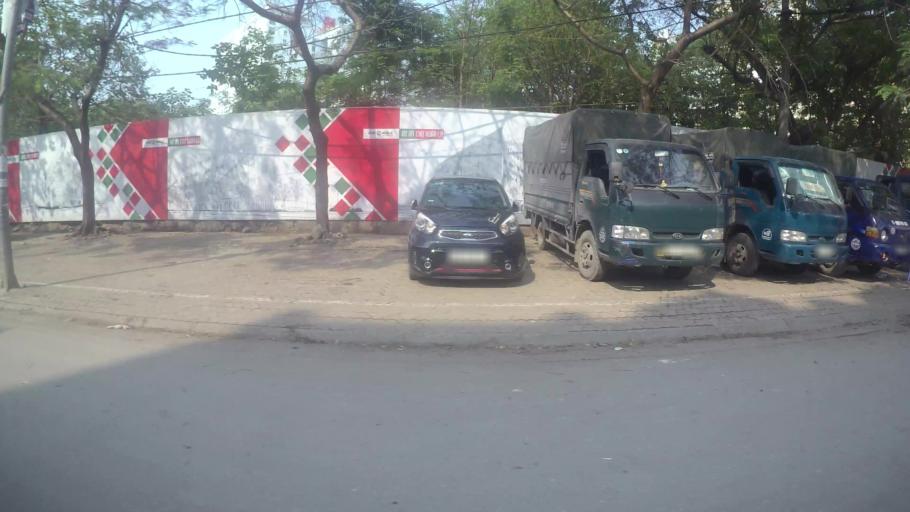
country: VN
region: Ha Noi
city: Tay Ho
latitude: 21.0630
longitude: 105.8075
